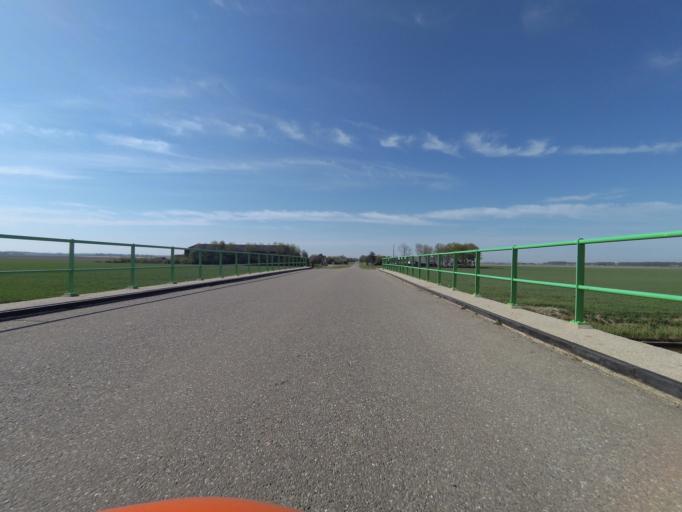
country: NL
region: Flevoland
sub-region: Gemeente Dronten
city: Dronten
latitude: 52.5710
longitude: 5.6942
